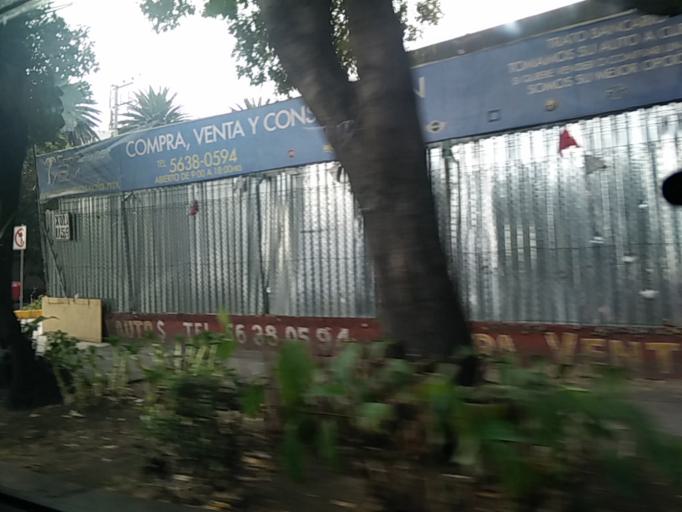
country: MX
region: Mexico City
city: Benito Juarez
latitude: 19.3959
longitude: -99.1572
